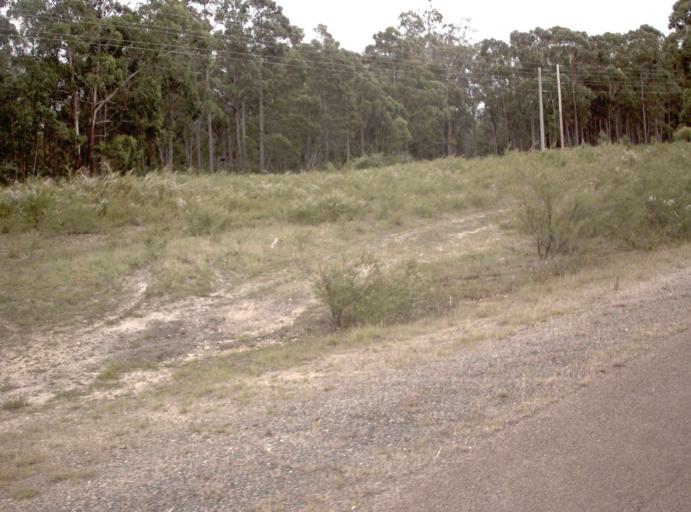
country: AU
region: Victoria
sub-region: East Gippsland
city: Lakes Entrance
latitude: -37.7162
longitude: 147.9611
